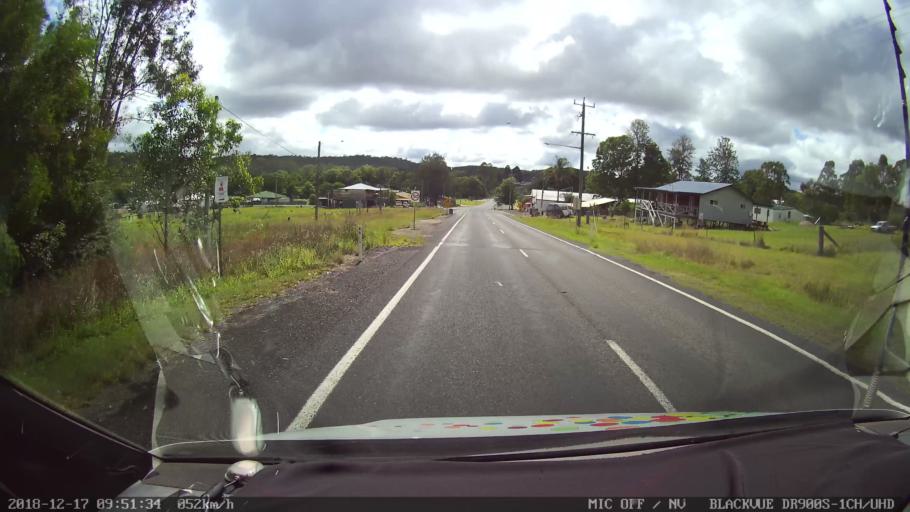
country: AU
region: New South Wales
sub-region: Tenterfield Municipality
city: Carrolls Creek
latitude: -28.9268
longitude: 152.3746
